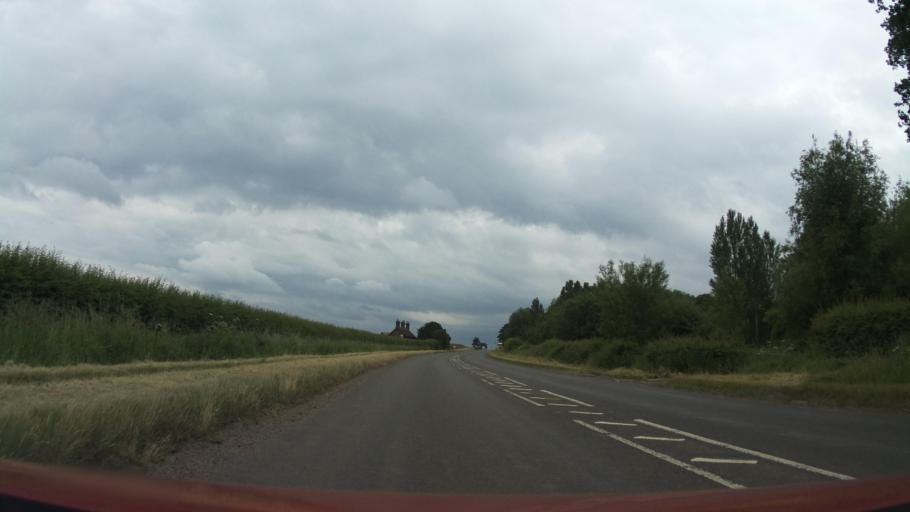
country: GB
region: England
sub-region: Staffordshire
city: Penkridge
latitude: 52.7446
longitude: -2.1078
